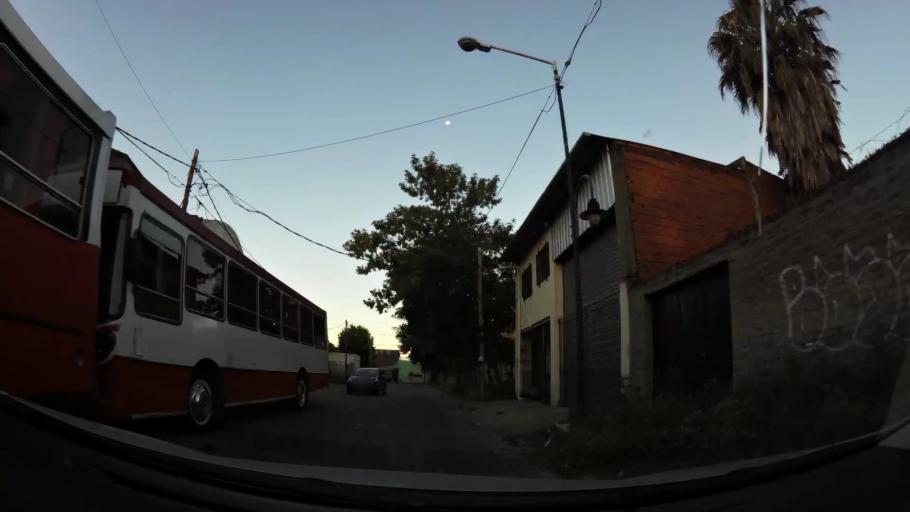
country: AR
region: Buenos Aires
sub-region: Partido de Tigre
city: Tigre
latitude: -34.4387
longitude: -58.5701
